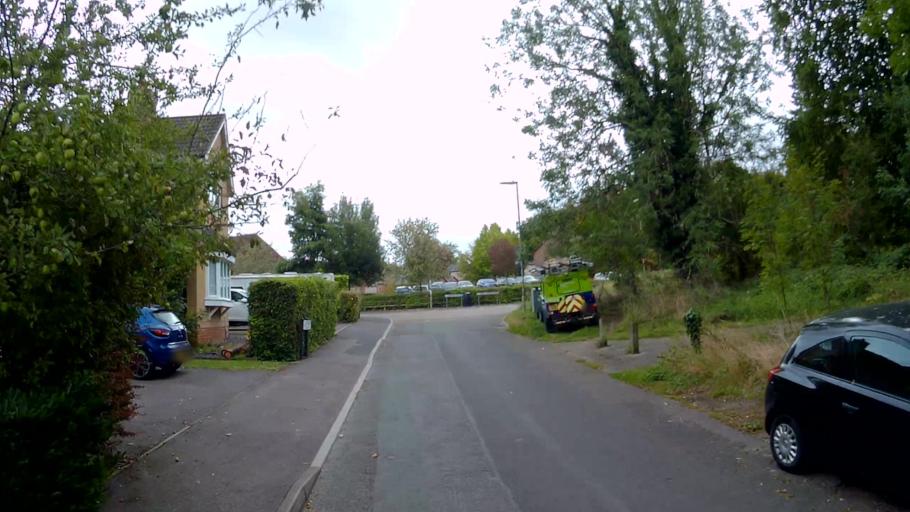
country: GB
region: England
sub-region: Hampshire
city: Basingstoke
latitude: 51.2358
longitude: -1.1200
